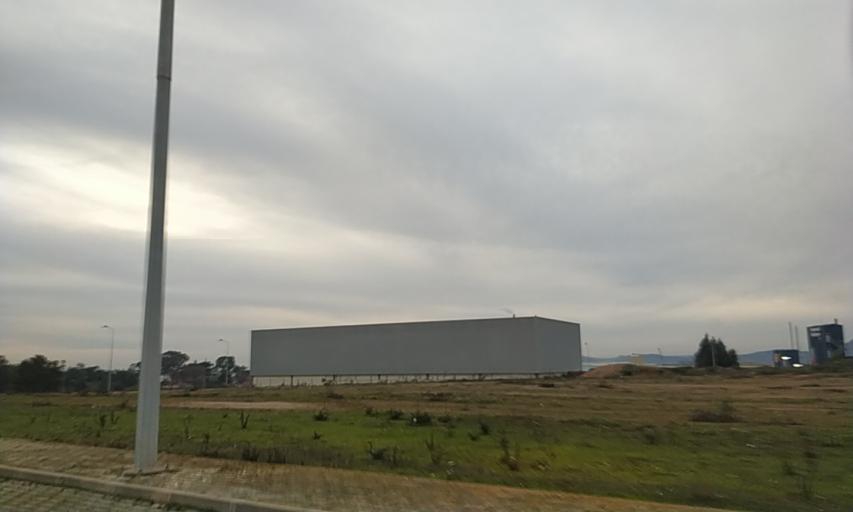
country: PT
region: Setubal
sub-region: Setubal
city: Setubal
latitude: 38.4993
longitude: -8.8270
